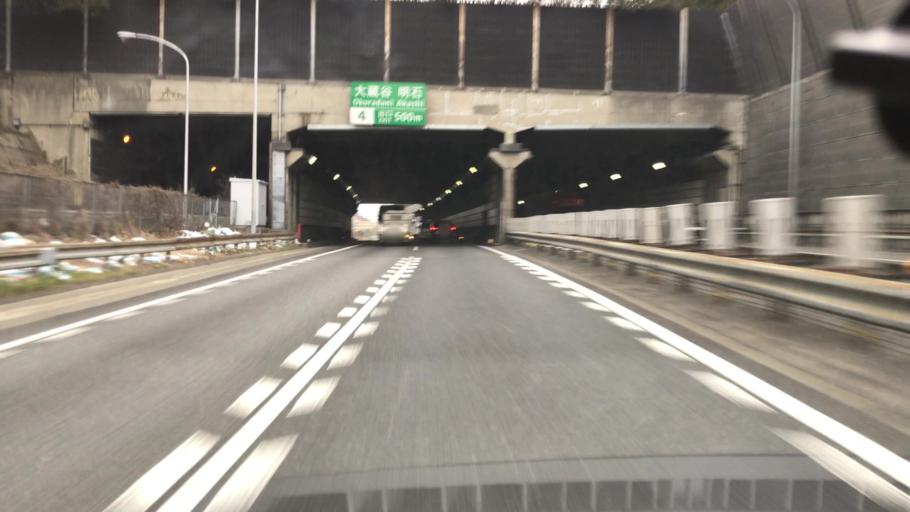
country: JP
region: Hyogo
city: Akashi
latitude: 34.6572
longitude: 135.0335
